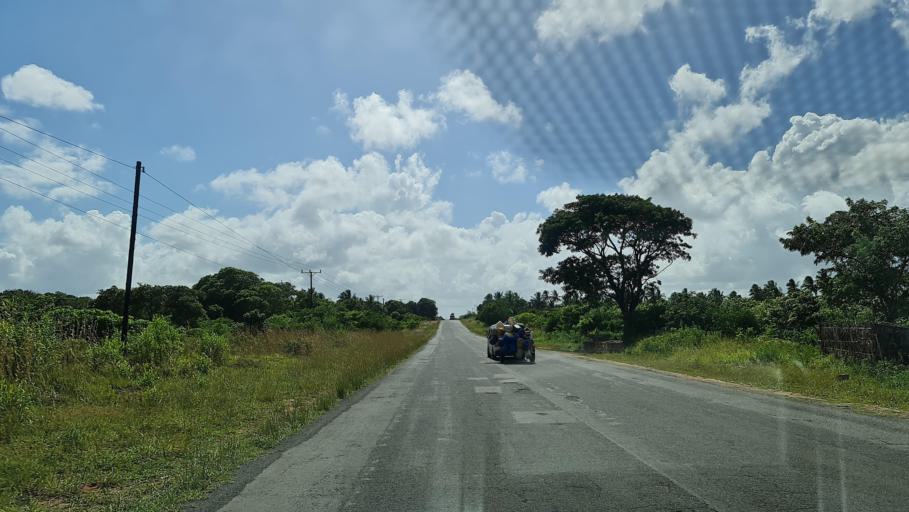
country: MZ
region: Gaza
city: Manjacaze
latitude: -24.6784
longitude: 34.5586
